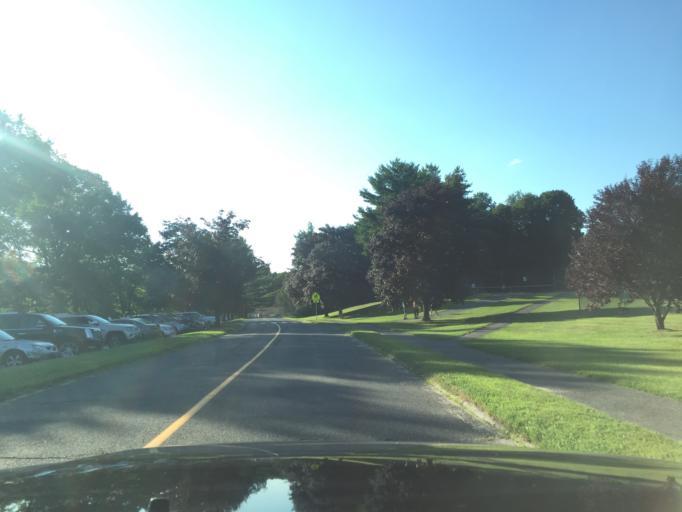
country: US
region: Connecticut
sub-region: Fairfield County
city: Bethel
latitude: 41.3810
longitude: -73.3950
